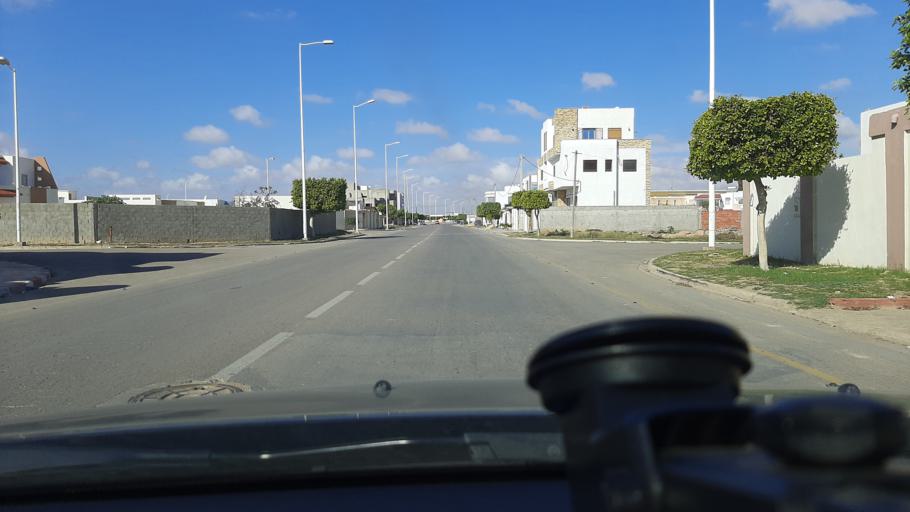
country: TN
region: Safaqis
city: Sfax
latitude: 34.8081
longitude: 10.7124
